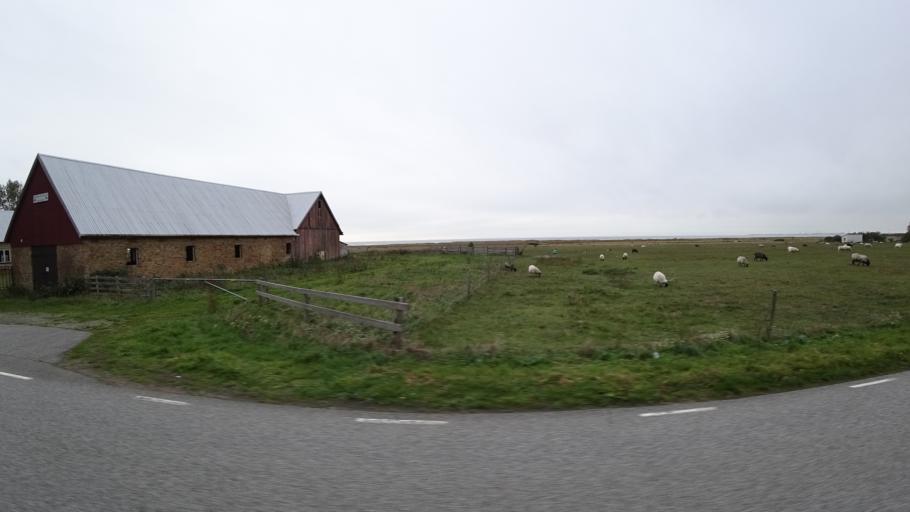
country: SE
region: Skane
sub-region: Kavlinge Kommun
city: Hofterup
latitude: 55.8129
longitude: 12.9366
